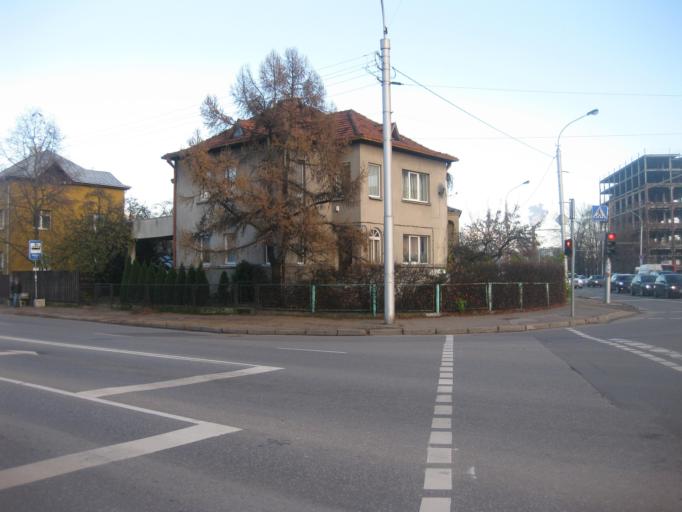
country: LT
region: Kauno apskritis
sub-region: Kaunas
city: Silainiai
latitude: 54.9156
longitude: 23.8929
